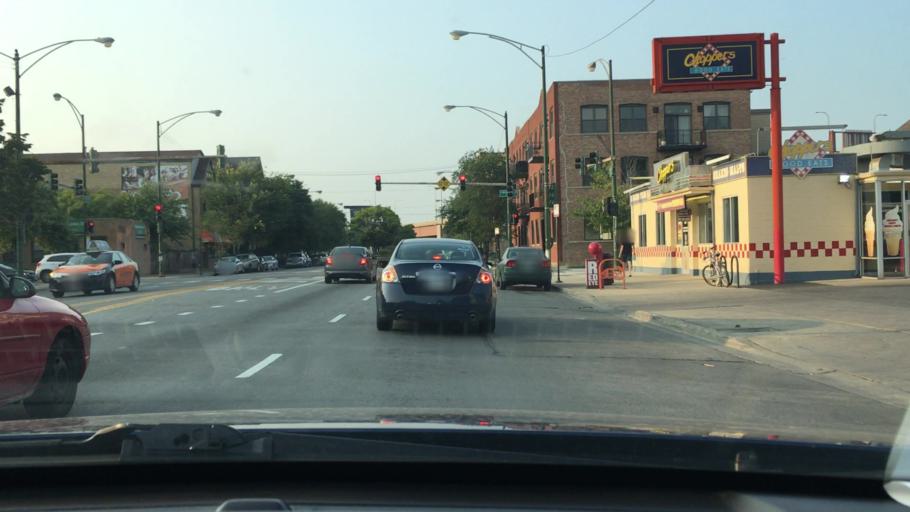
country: US
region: Illinois
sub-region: Cook County
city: Chicago
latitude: 41.9120
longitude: -87.6676
